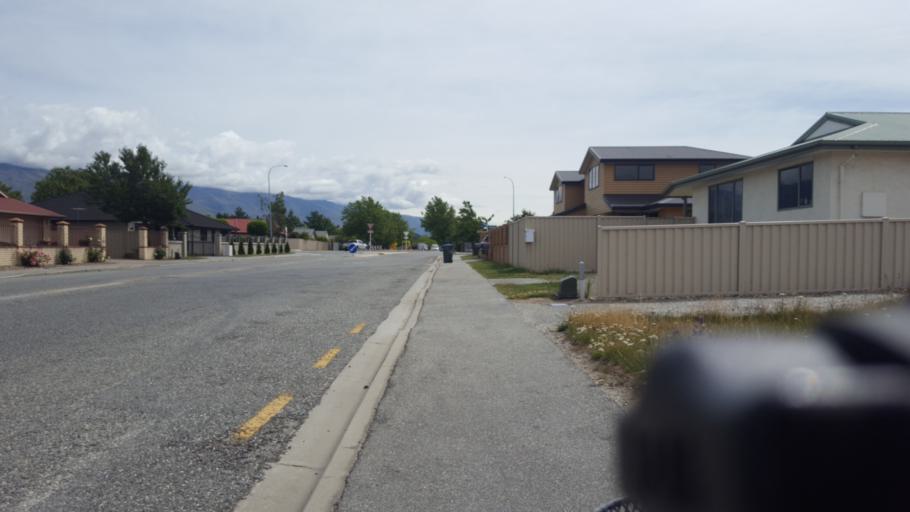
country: NZ
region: Otago
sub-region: Queenstown-Lakes District
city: Wanaka
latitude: -45.0467
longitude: 169.1954
